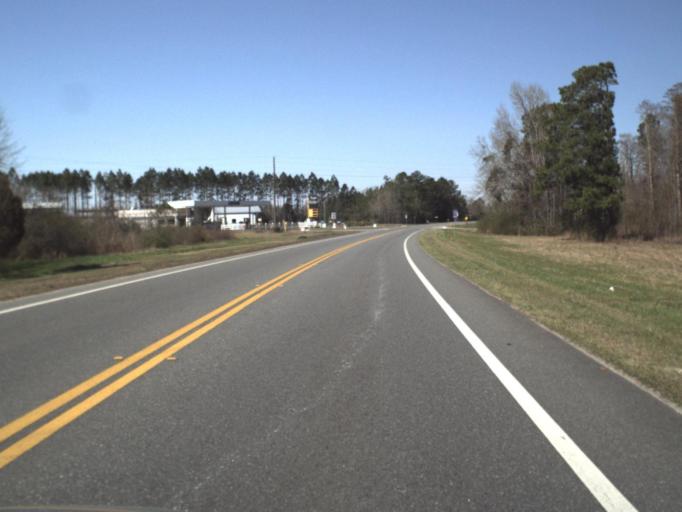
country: US
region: Florida
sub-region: Jackson County
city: Sneads
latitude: 30.7216
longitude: -85.0771
